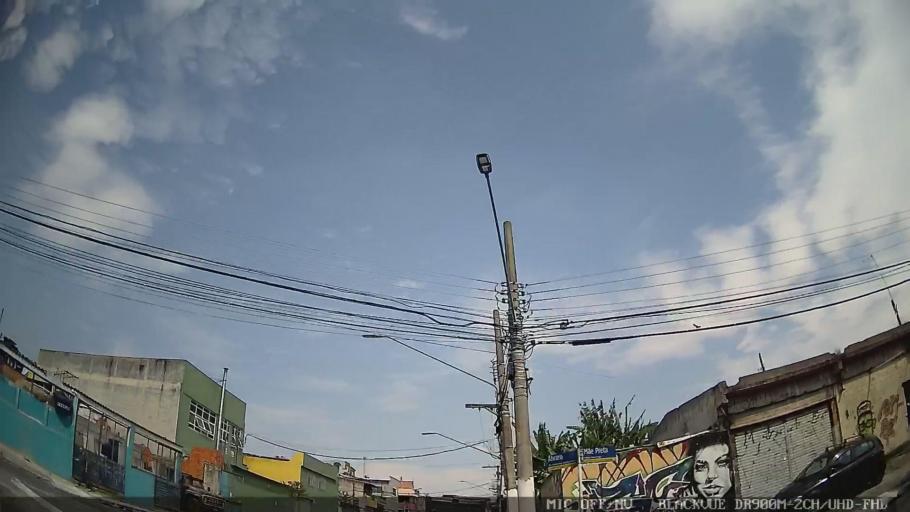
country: BR
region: Sao Paulo
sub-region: Ferraz De Vasconcelos
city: Ferraz de Vasconcelos
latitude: -23.5100
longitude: -46.4166
